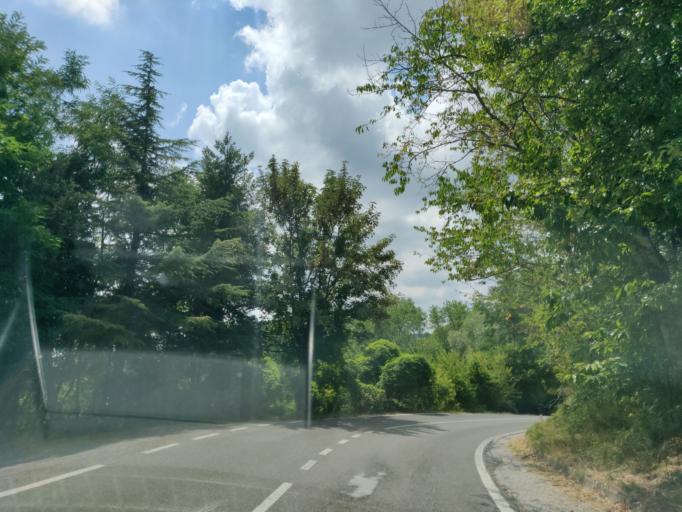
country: IT
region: Tuscany
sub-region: Provincia di Siena
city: Abbadia San Salvatore
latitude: 42.8933
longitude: 11.6576
